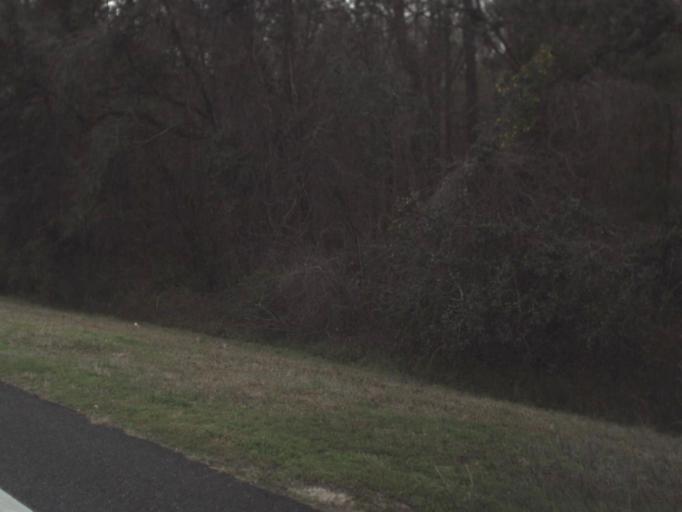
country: US
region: Florida
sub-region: Jefferson County
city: Monticello
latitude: 30.3730
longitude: -83.8093
